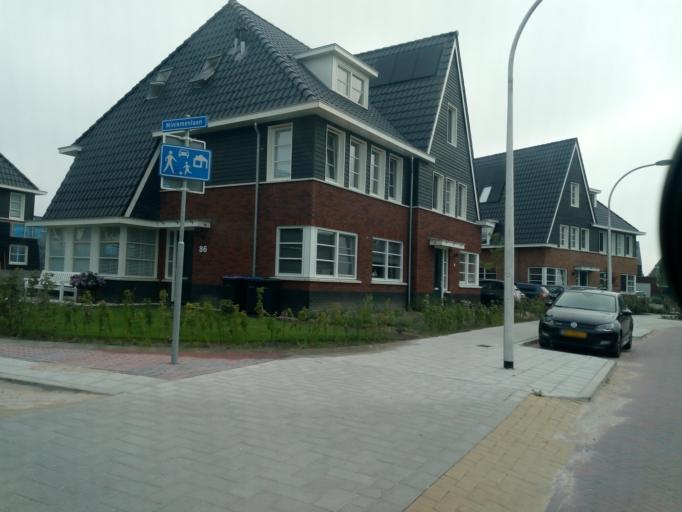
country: NL
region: South Holland
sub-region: Gemeente Alphen aan den Rijn
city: Alphen aan den Rijn
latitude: 52.1136
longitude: 4.6509
